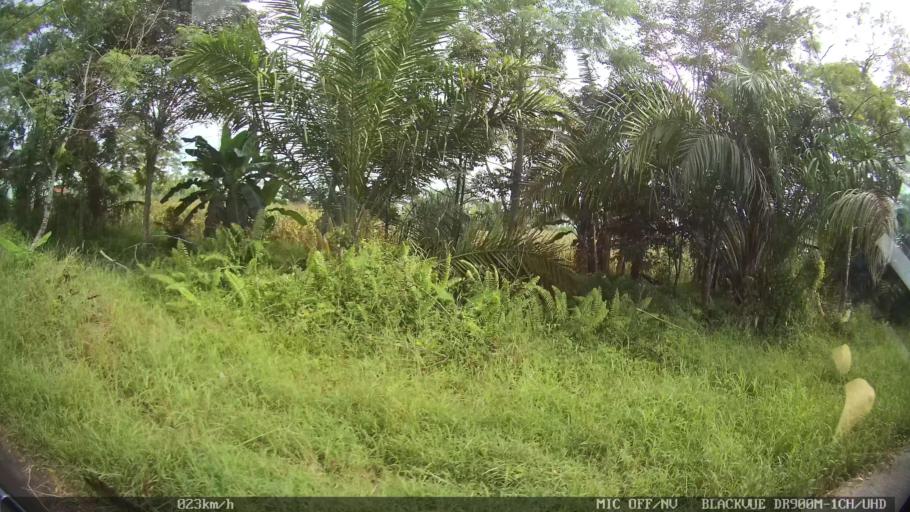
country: ID
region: North Sumatra
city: Percut
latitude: 3.6201
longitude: 98.7628
